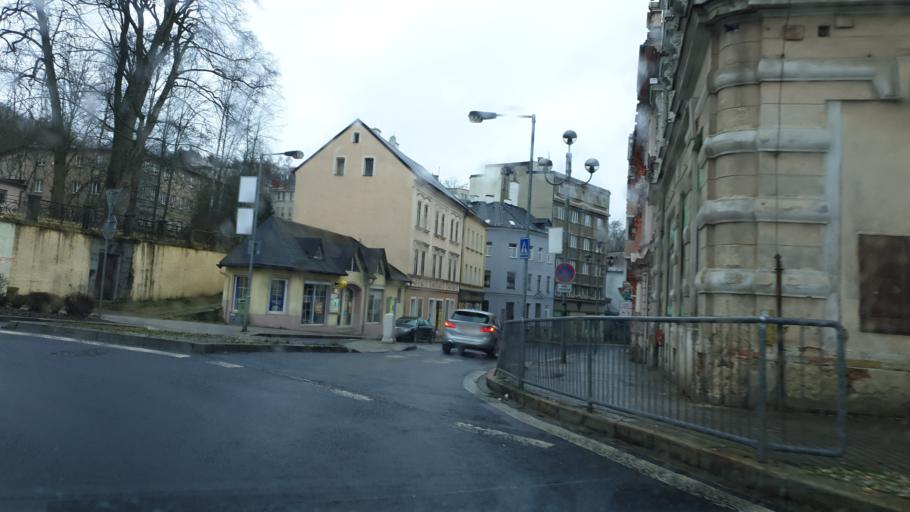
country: CZ
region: Karlovarsky
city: As
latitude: 50.2216
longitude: 12.1879
